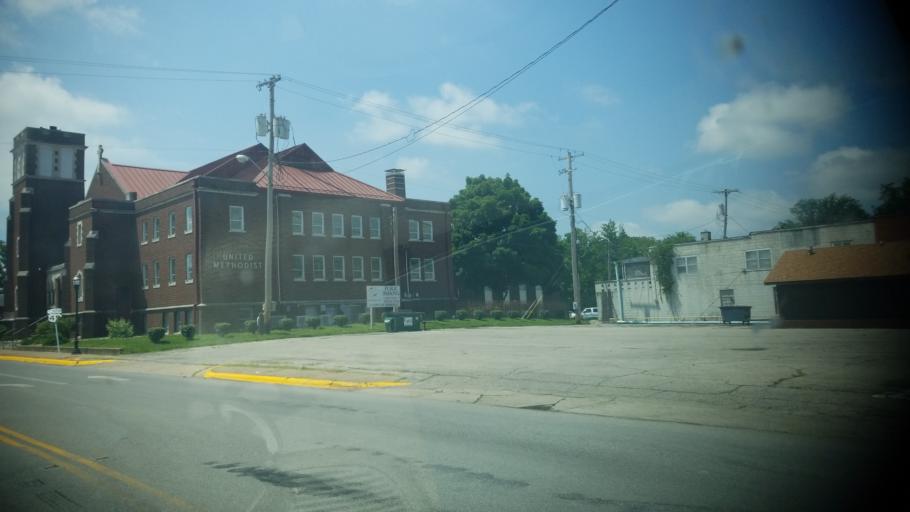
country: US
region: Illinois
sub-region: Wayne County
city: Fairfield
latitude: 38.3795
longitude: -88.3599
